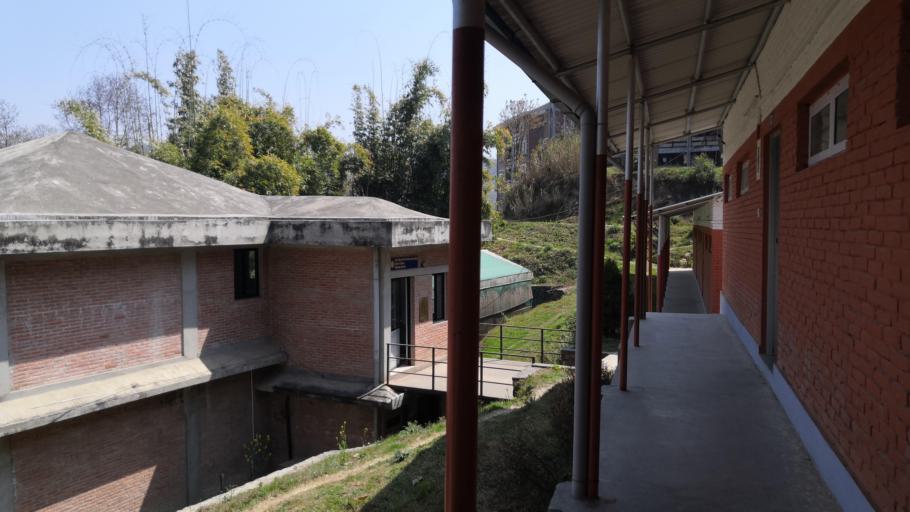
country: NP
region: Central Region
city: Banepa
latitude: 27.6185
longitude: 85.5396
